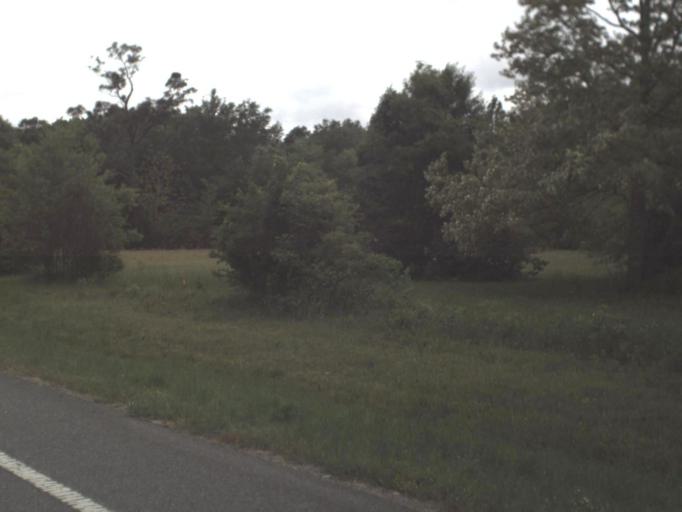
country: US
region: Florida
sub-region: Santa Rosa County
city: Point Baker
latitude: 30.7967
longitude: -87.0922
